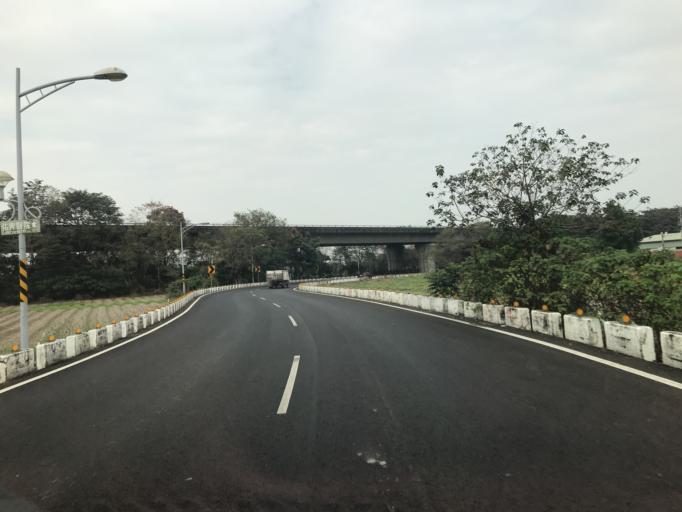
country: TW
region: Taiwan
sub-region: Pingtung
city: Pingtung
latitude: 22.6386
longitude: 120.5391
